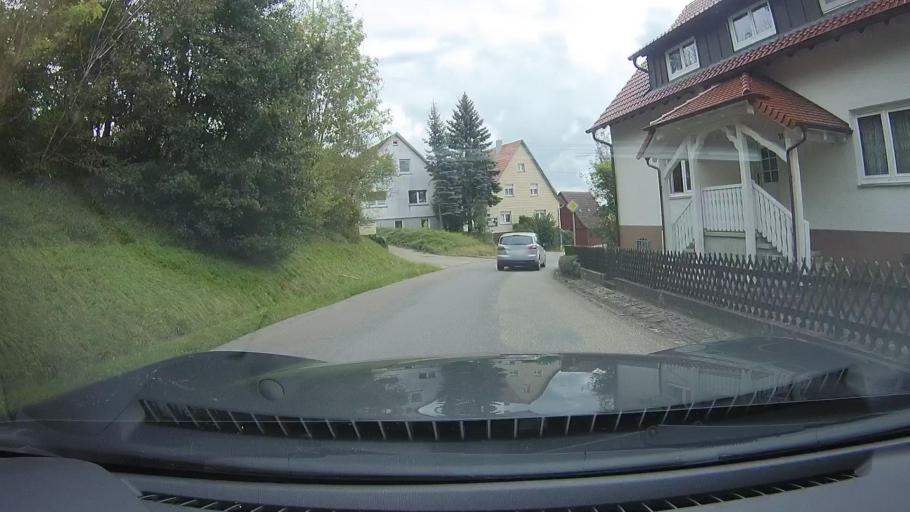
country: DE
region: Baden-Wuerttemberg
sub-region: Regierungsbezirk Stuttgart
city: Murrhardt
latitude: 49.0034
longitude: 9.5652
